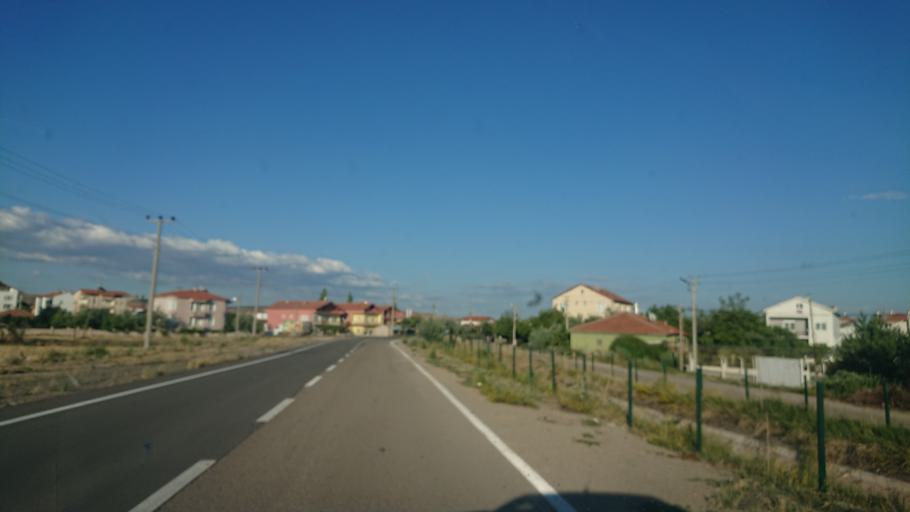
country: TR
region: Aksaray
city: Aksaray
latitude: 38.3913
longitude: 33.9908
